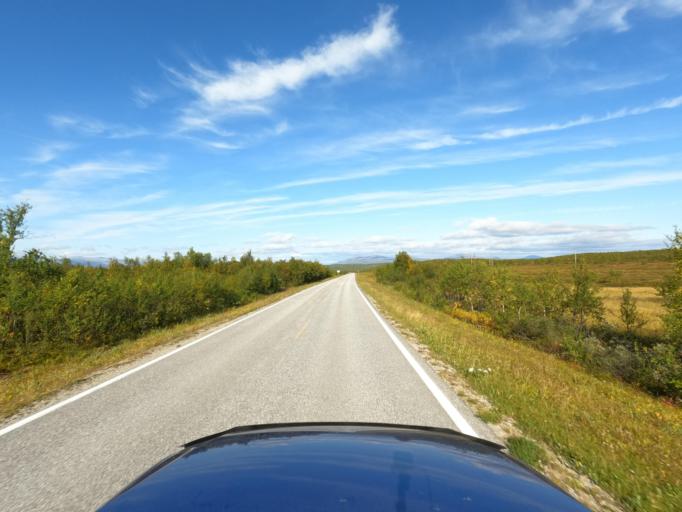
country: NO
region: Finnmark Fylke
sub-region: Karasjok
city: Karasjohka
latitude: 69.7274
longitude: 25.2344
